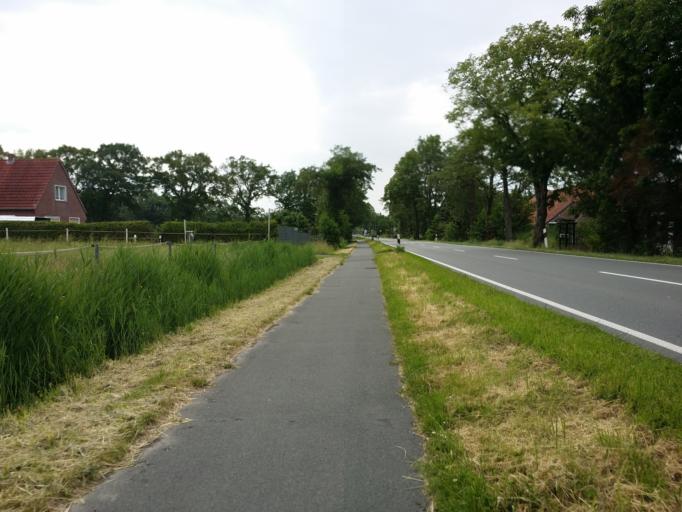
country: DE
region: Lower Saxony
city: Wittmund
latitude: 53.5451
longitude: 7.7823
